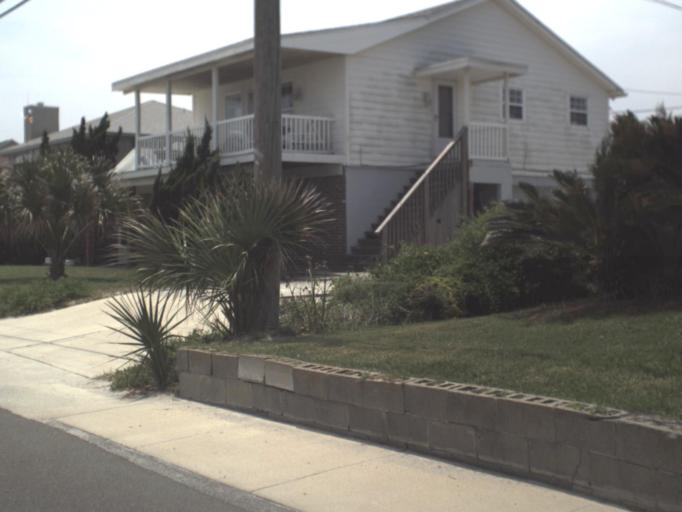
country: US
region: Florida
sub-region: Nassau County
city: Fernandina Beach
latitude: 30.6584
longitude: -81.4327
